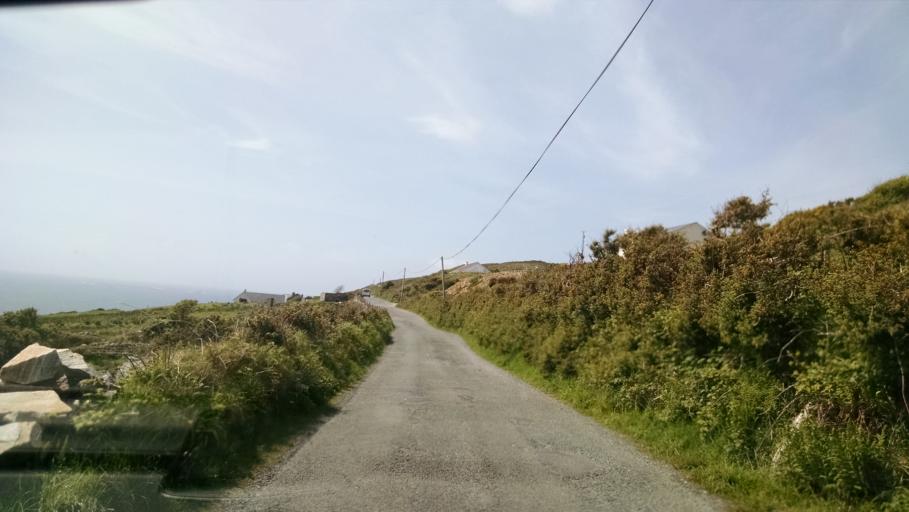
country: IE
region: Connaught
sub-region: County Galway
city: Clifden
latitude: 53.4942
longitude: -10.0666
